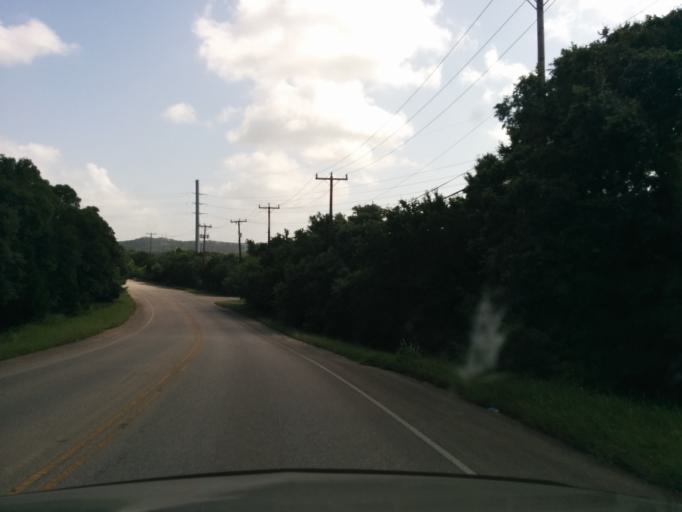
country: US
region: Texas
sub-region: Bexar County
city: Cross Mountain
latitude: 29.5985
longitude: -98.6295
